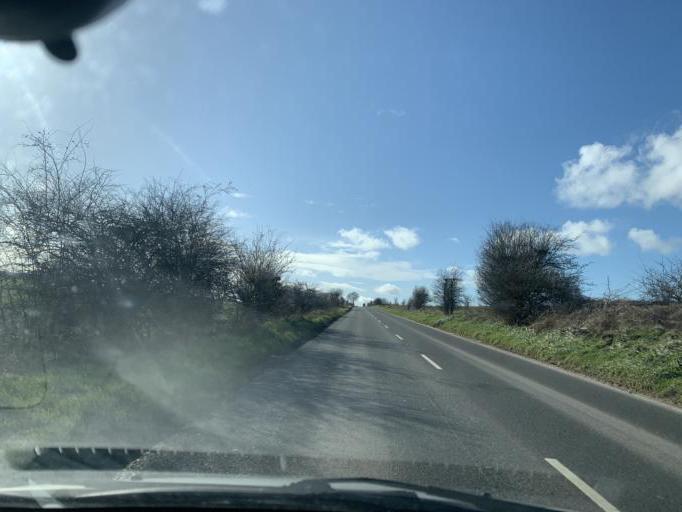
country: GB
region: England
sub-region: Wiltshire
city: Shrewton
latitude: 51.1908
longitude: -1.9644
